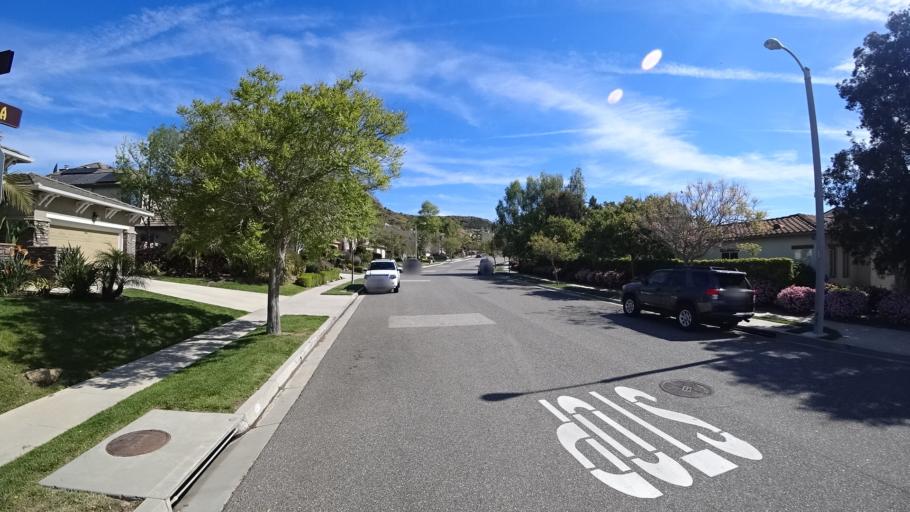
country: US
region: California
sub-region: Ventura County
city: Casa Conejo
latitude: 34.1724
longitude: -118.9693
